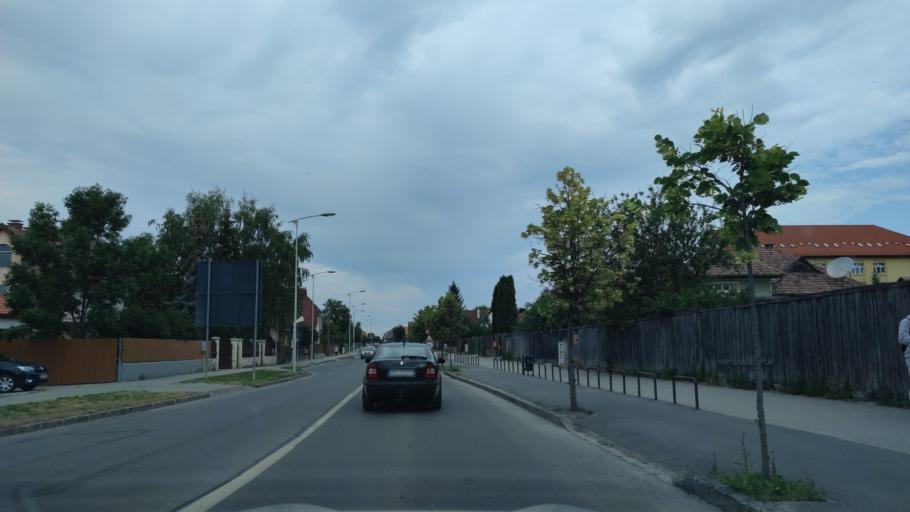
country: RO
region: Harghita
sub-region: Municipiul Miercurea Ciuc
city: Miercurea-Ciuc
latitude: 46.3692
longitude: 25.8057
